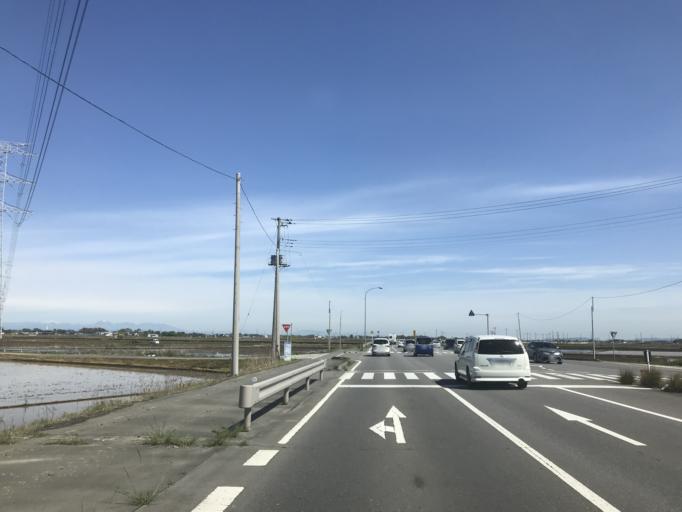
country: JP
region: Ibaraki
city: Ishige
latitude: 36.1255
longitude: 139.9821
